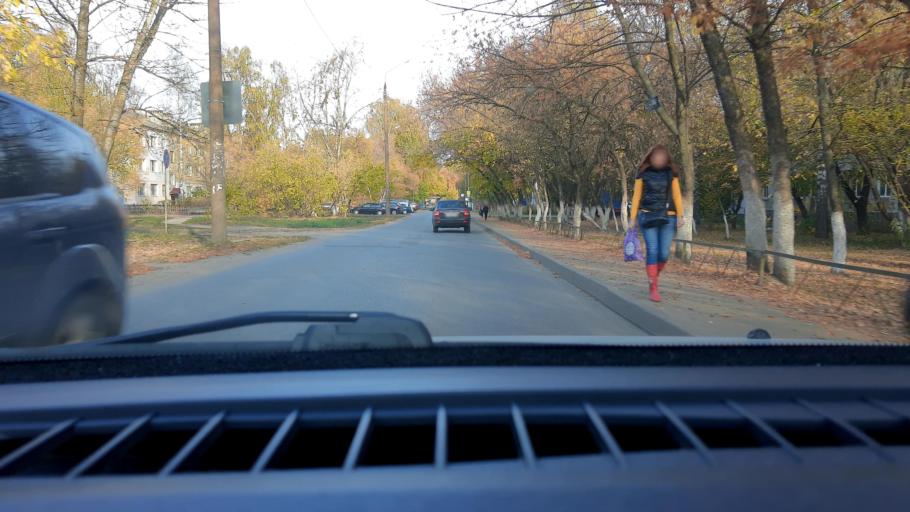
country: RU
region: Nizjnij Novgorod
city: Gorbatovka
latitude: 56.3546
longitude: 43.8352
